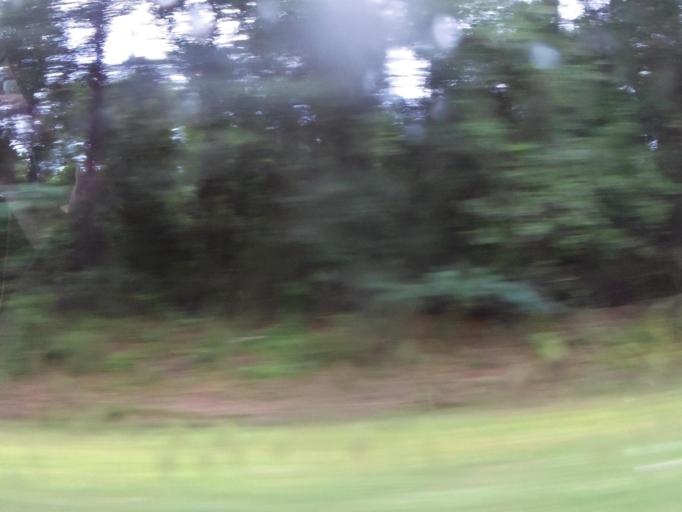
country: US
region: Florida
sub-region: Baker County
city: Macclenny
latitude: 30.2662
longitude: -82.1622
